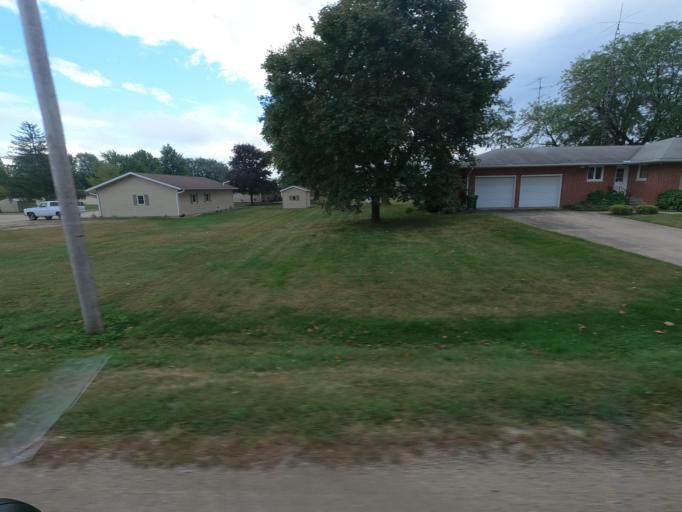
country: US
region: Iowa
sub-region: Henry County
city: Mount Pleasant
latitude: 40.7846
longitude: -91.6060
